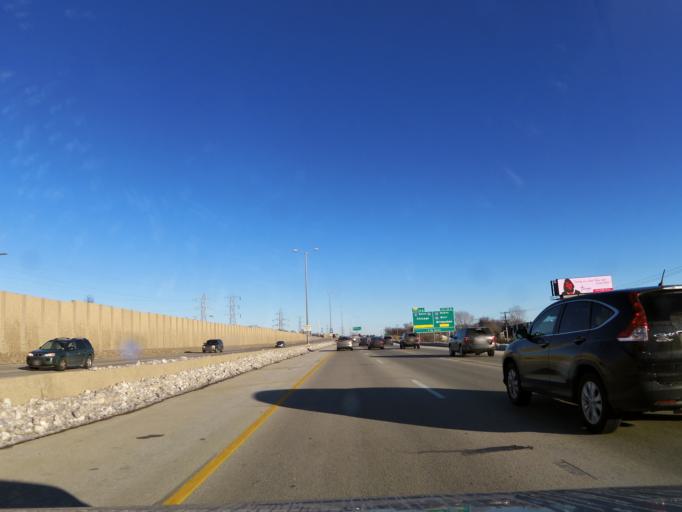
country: US
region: Wisconsin
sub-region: Milwaukee County
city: Greendale
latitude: 42.9624
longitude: -87.9836
